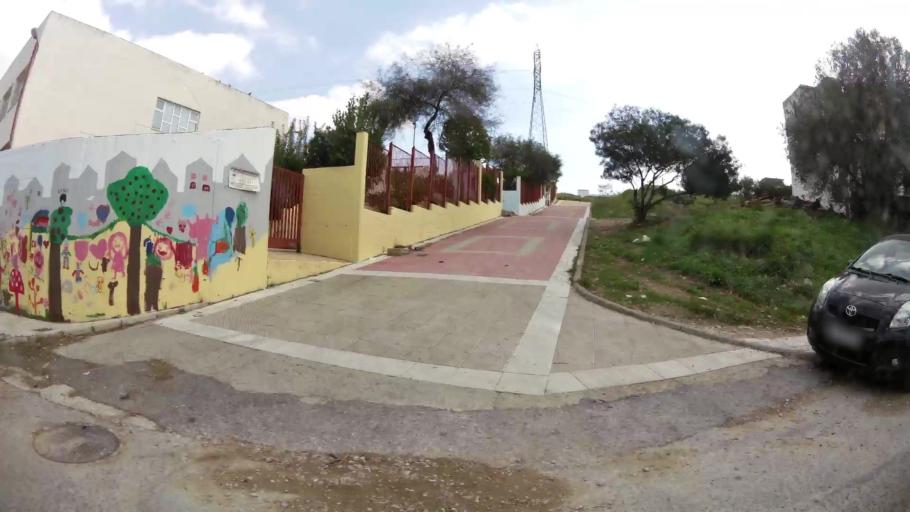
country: GR
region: Attica
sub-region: Nomarchia Dytikis Attikis
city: Zefyri
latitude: 38.0585
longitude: 23.7201
